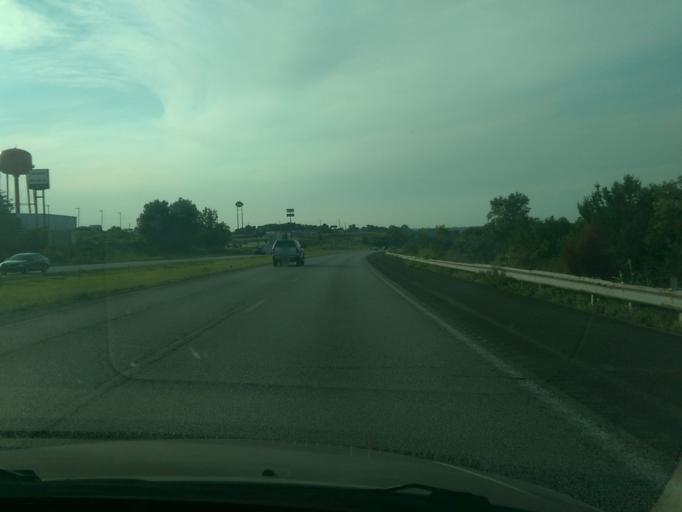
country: US
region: Missouri
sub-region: Platte County
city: Platte City
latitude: 39.3577
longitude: -94.7662
